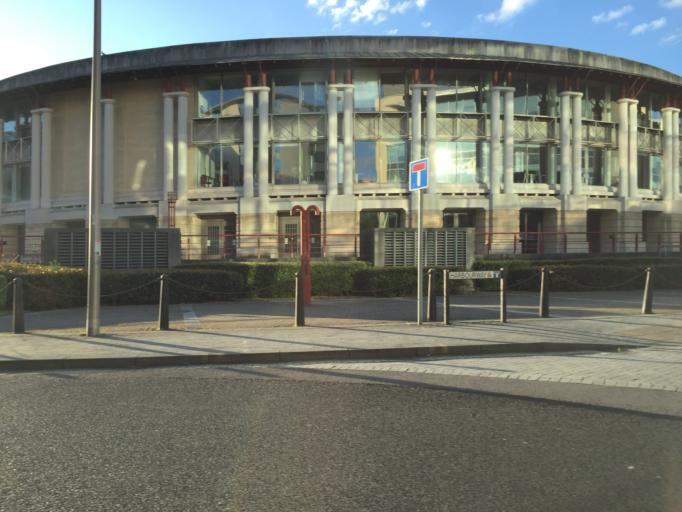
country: GB
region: England
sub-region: Bristol
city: Bristol
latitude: 51.4491
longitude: -2.6026
